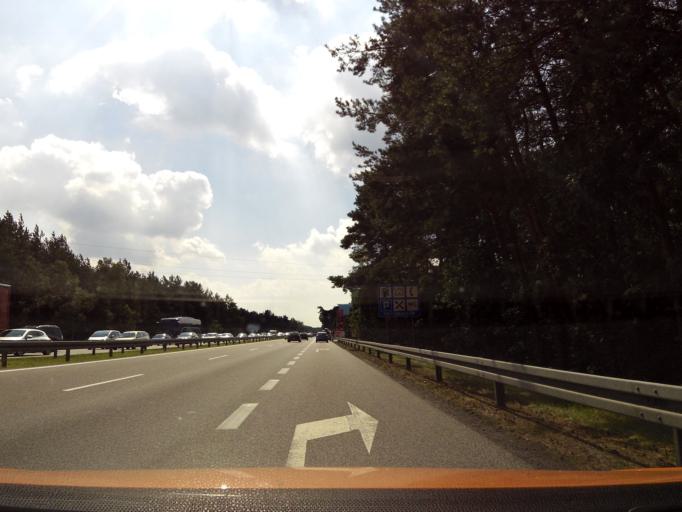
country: PL
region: West Pomeranian Voivodeship
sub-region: Powiat goleniowski
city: Goleniow
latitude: 53.4660
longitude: 14.7873
